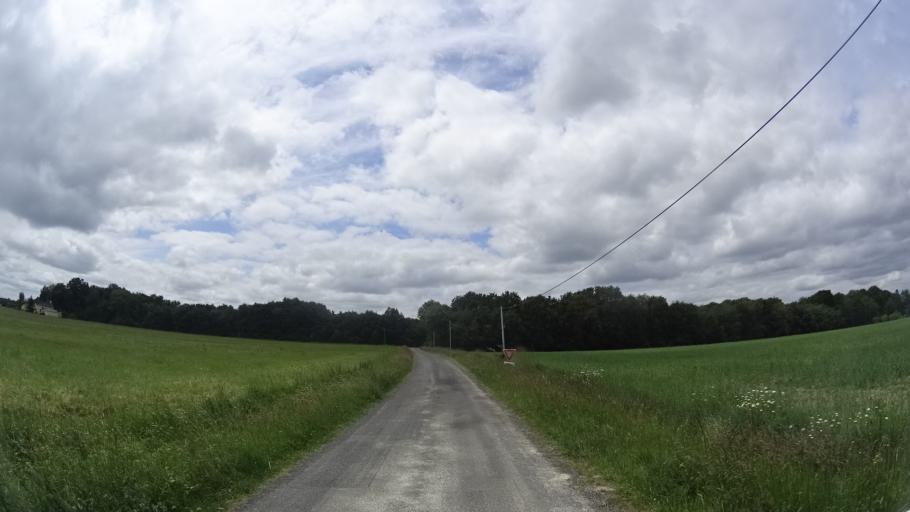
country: FR
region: Pays de la Loire
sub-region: Departement de Maine-et-Loire
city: Chenehutte-Treves-Cunault
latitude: 47.2993
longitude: -0.1550
